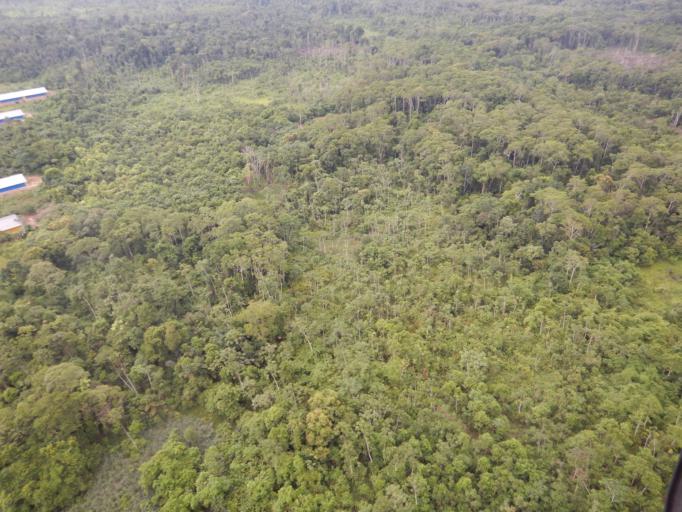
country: BO
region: Cochabamba
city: Chimore
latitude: -16.9991
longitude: -65.0675
